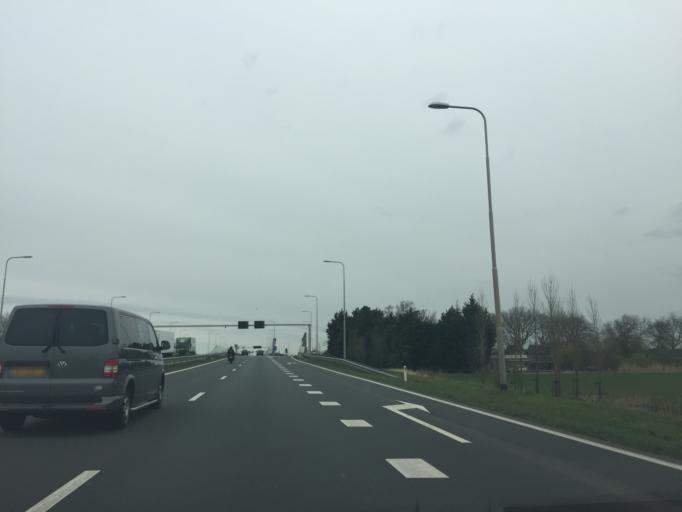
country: NL
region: North Holland
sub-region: Gemeente Aalsmeer
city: Aalsmeer
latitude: 52.2673
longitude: 4.7902
